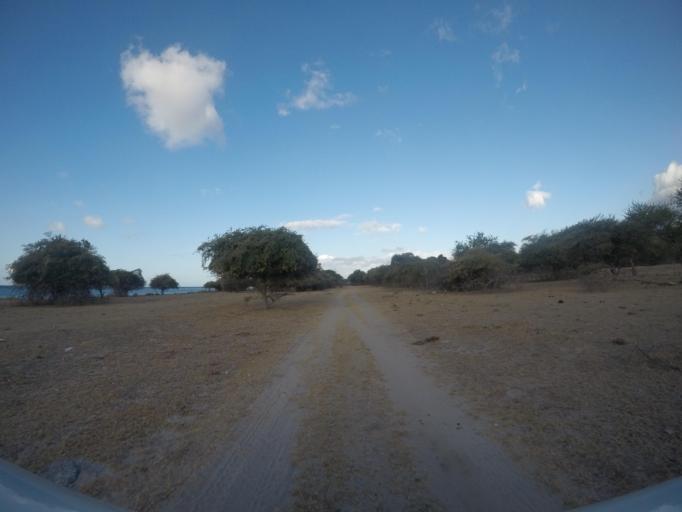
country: TL
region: Lautem
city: Lospalos
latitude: -8.3246
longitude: 126.9900
